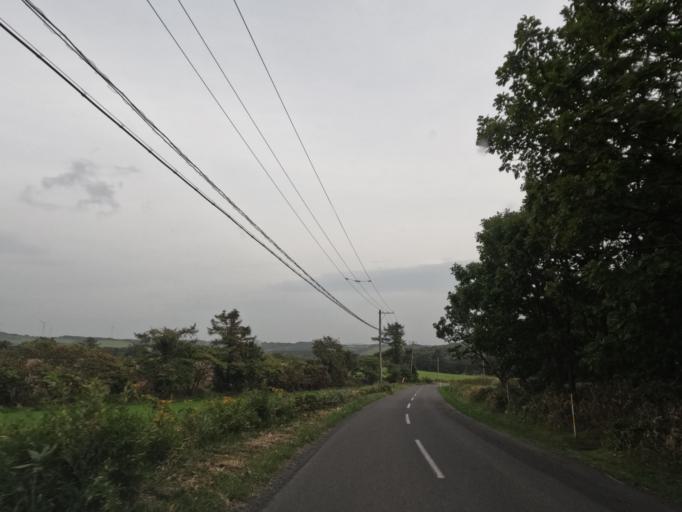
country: JP
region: Hokkaido
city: Date
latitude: 42.4055
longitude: 140.9237
